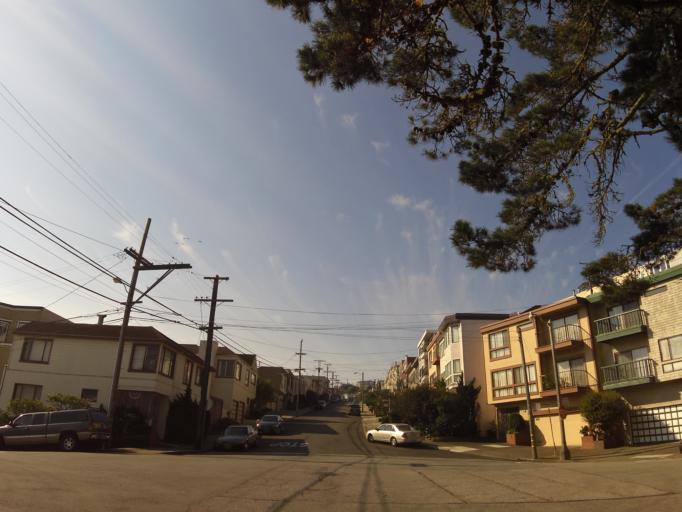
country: US
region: California
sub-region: San Mateo County
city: Daly City
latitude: 37.7548
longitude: -122.4678
